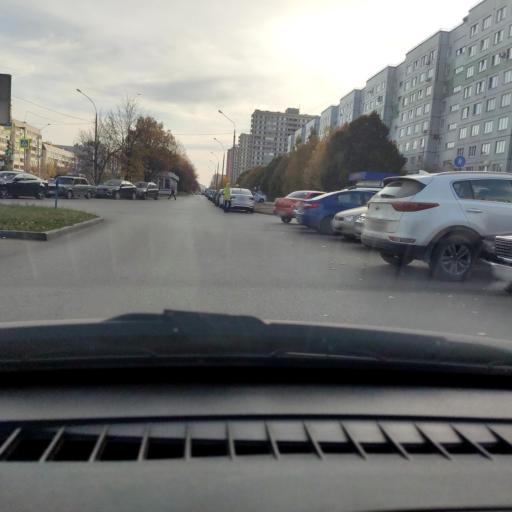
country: RU
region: Samara
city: Tol'yatti
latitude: 53.5430
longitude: 49.3208
